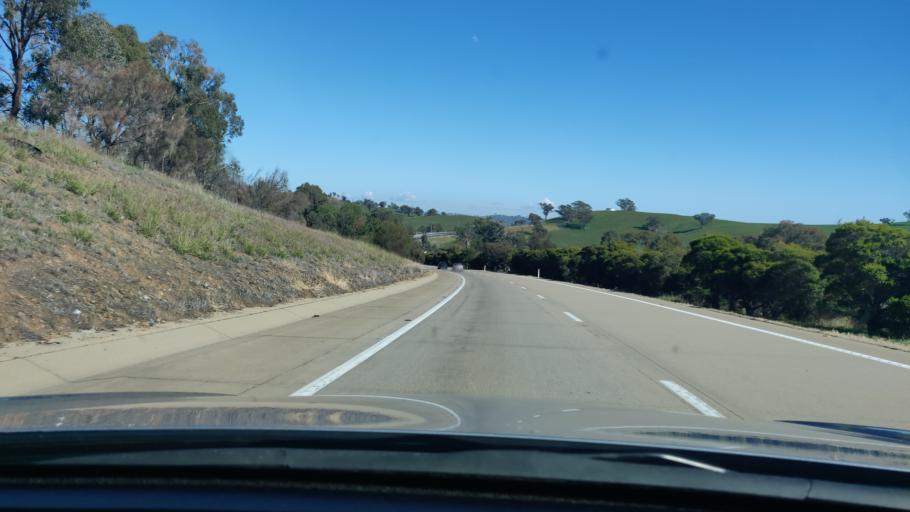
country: AU
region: New South Wales
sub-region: Wagga Wagga
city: Forest Hill
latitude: -35.2162
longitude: 147.7992
